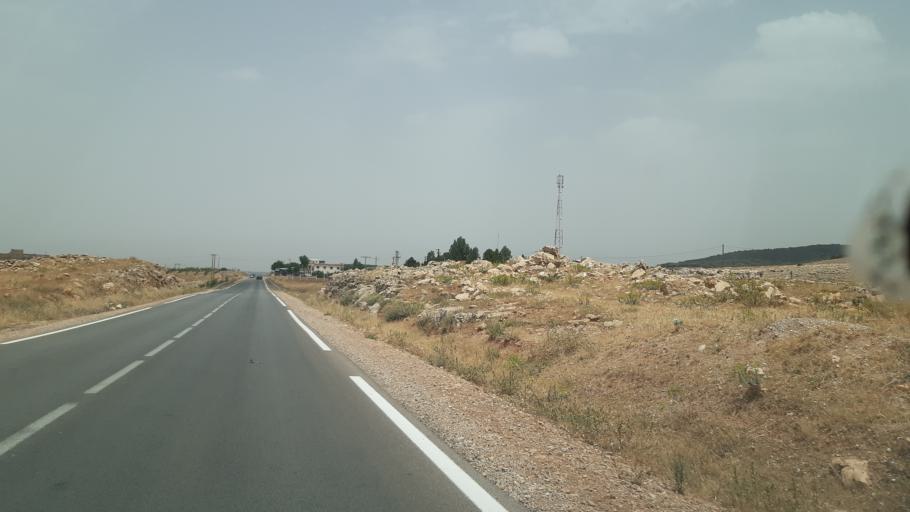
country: MA
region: Meknes-Tafilalet
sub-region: Ifrane
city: Ifrane
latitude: 33.6136
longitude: -5.0813
